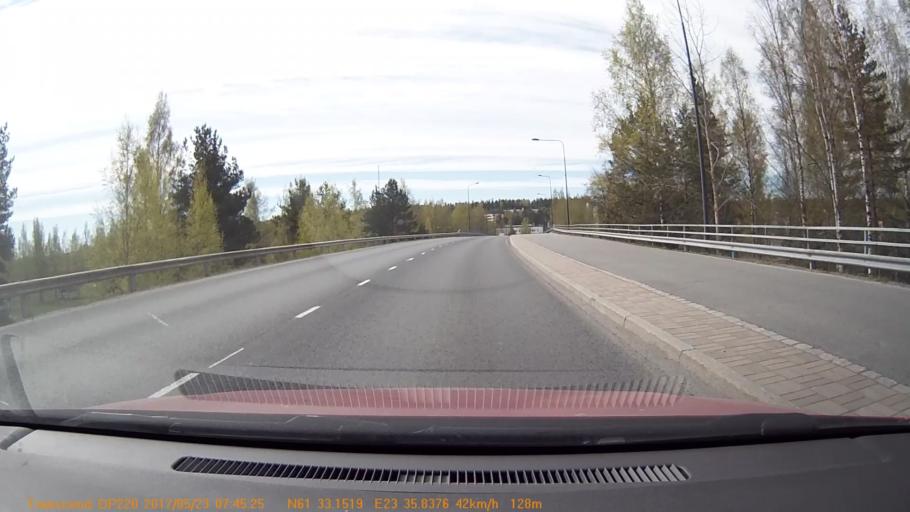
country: FI
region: Pirkanmaa
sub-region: Tampere
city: Yloejaervi
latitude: 61.5527
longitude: 23.5974
